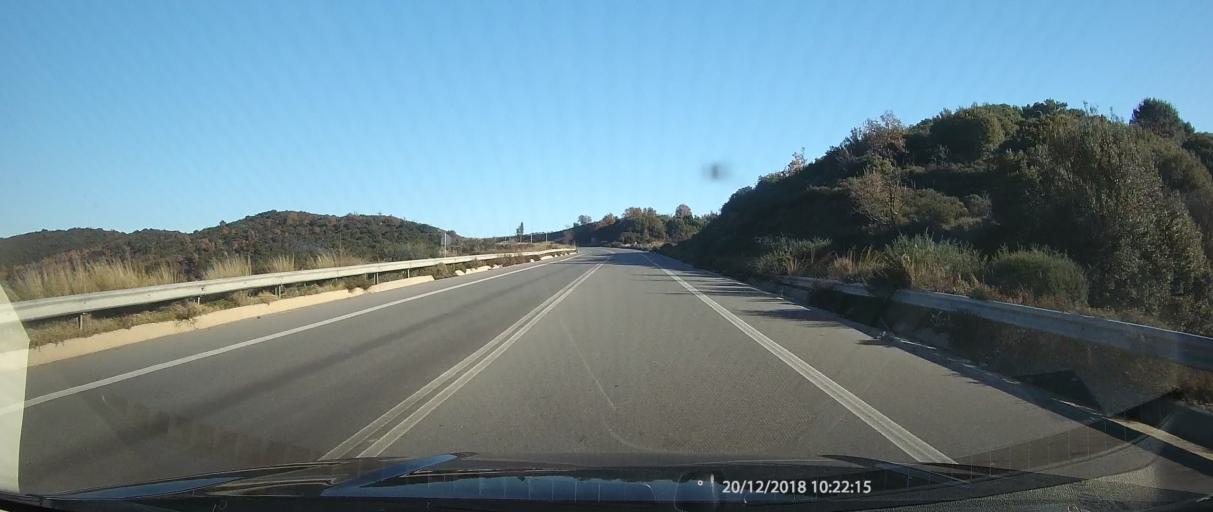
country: GR
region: Peloponnese
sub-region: Nomos Lakonias
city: Magoula
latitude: 37.1717
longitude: 22.4278
